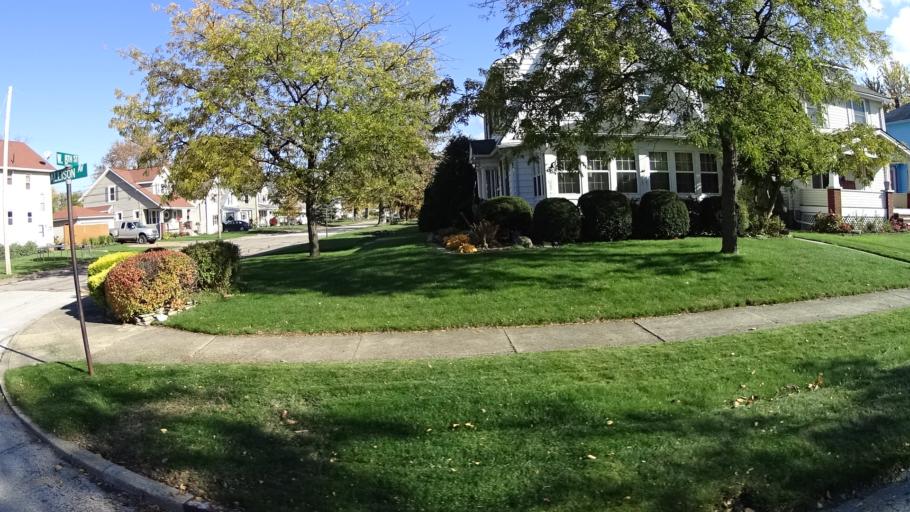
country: US
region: Ohio
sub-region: Lorain County
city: Lorain
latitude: 41.4615
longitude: -82.1898
